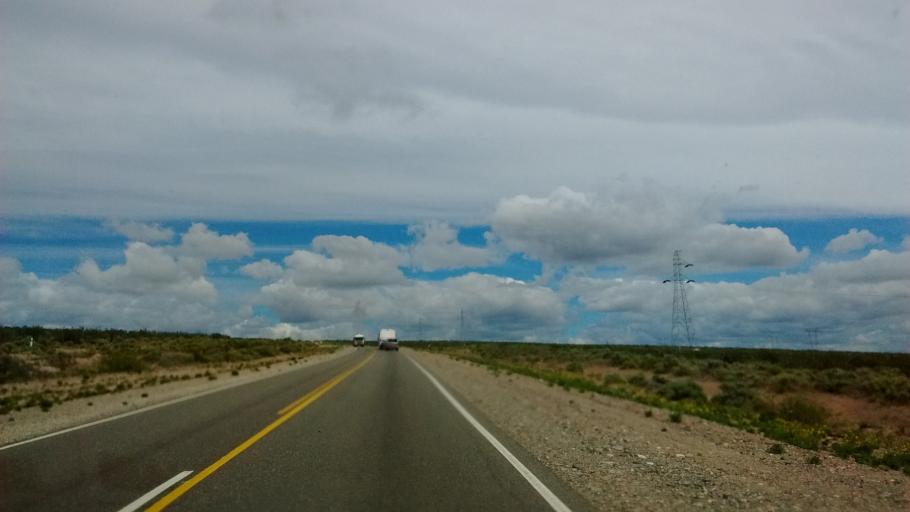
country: AR
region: Neuquen
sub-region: Departamento de Picun Leufu
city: Picun Leufu
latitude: -39.7324
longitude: -69.5818
